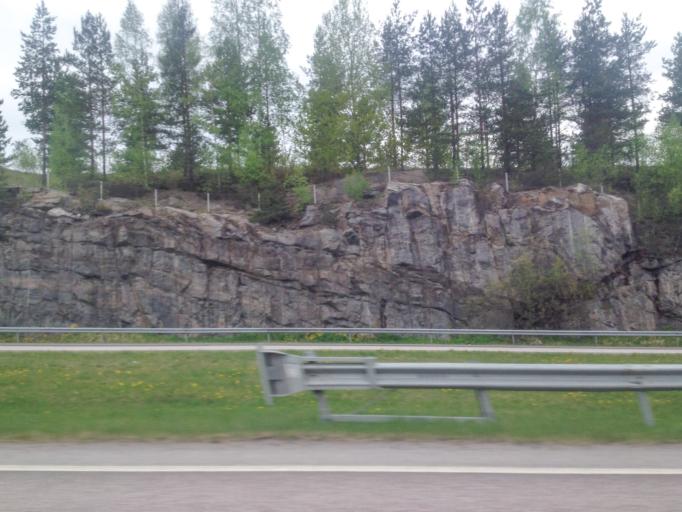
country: FI
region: Uusimaa
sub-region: Helsinki
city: Nurmijaervi
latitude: 60.4550
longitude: 24.8464
